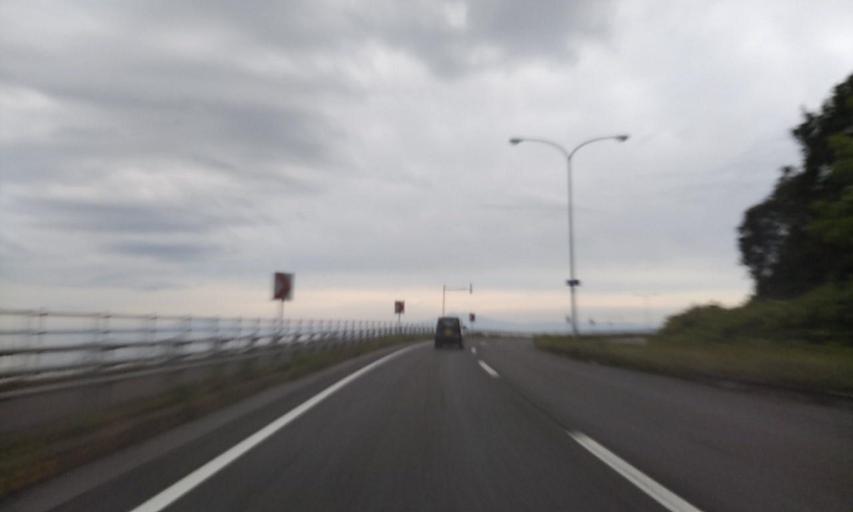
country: JP
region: Hokkaido
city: Abashiri
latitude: 44.0021
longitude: 144.2886
